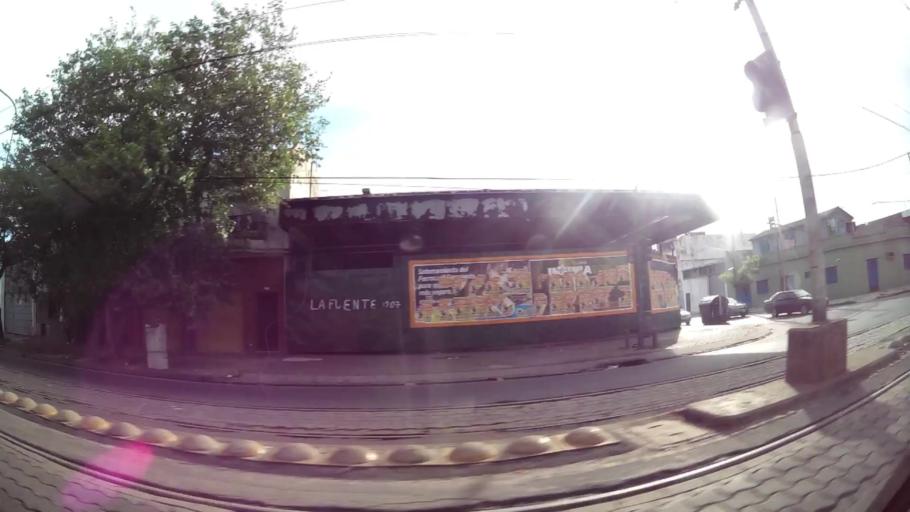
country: AR
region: Buenos Aires F.D.
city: Villa Lugano
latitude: -34.6447
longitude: -58.4604
